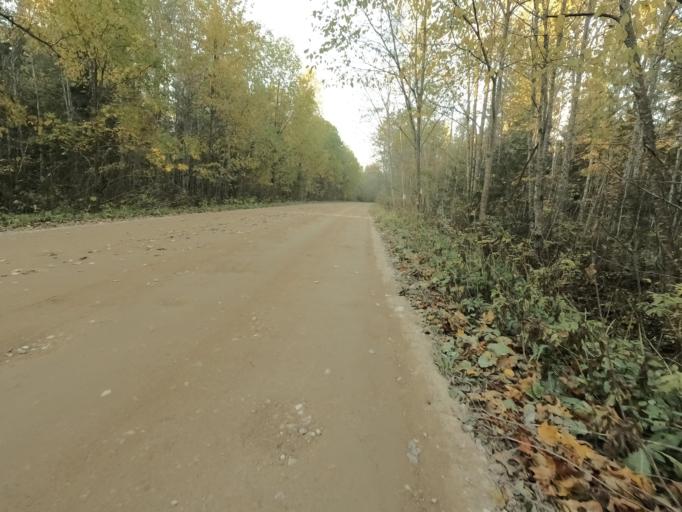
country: RU
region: Leningrad
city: Lyuban'
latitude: 58.9838
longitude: 31.0985
